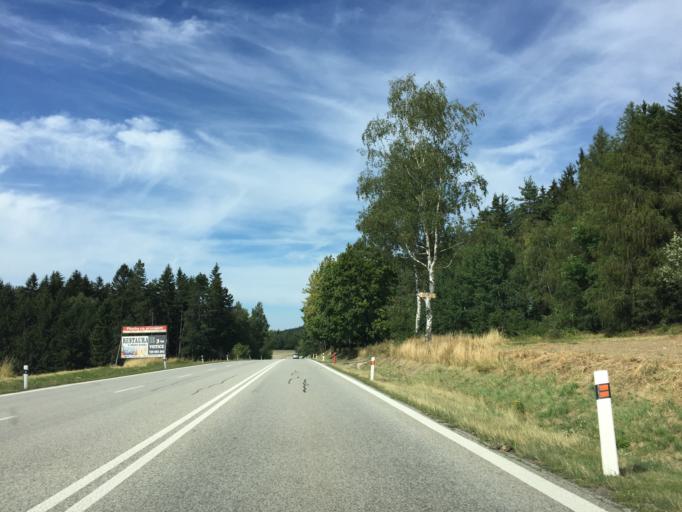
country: CZ
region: Central Bohemia
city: Votice
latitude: 49.6039
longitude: 14.6600
